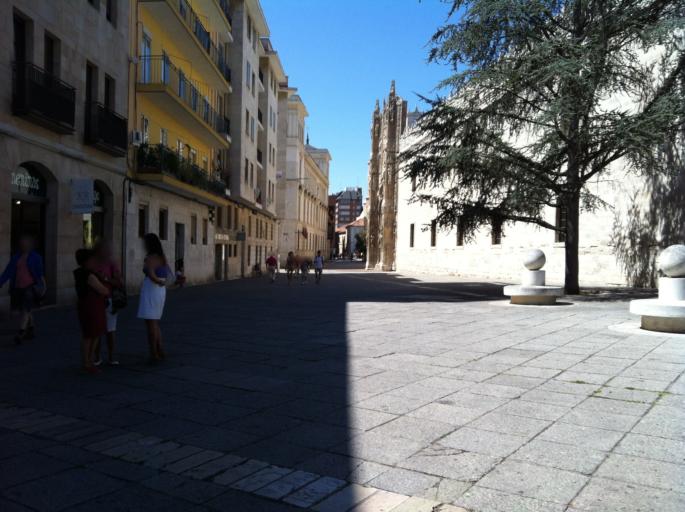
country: ES
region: Castille and Leon
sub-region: Provincia de Valladolid
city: Valladolid
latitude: 41.6575
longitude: -4.7229
